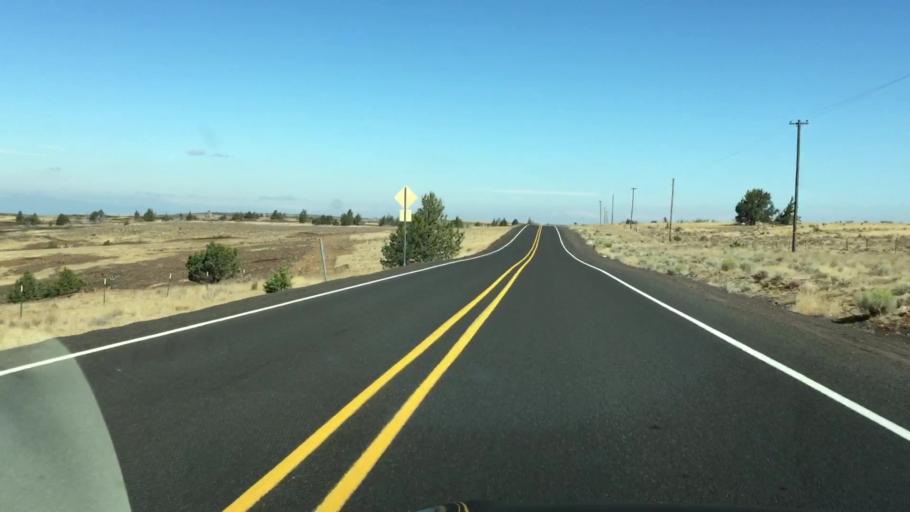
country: US
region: Oregon
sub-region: Jefferson County
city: Warm Springs
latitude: 45.0185
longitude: -120.9899
